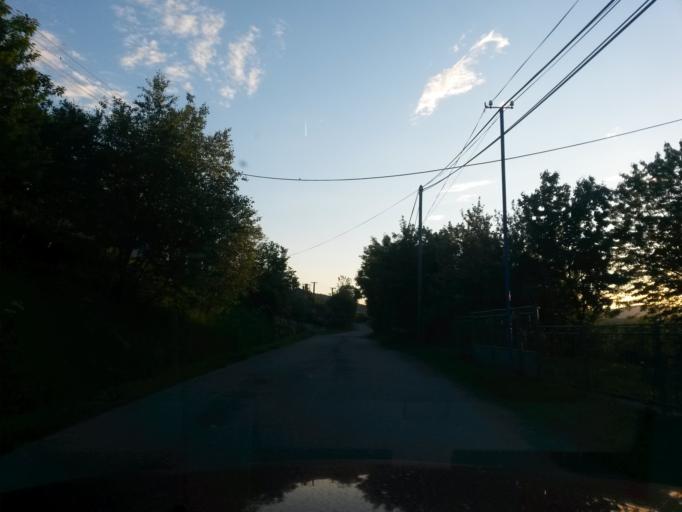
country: UA
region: Zakarpattia
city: Velykyi Bereznyi
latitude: 48.8222
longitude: 22.3551
